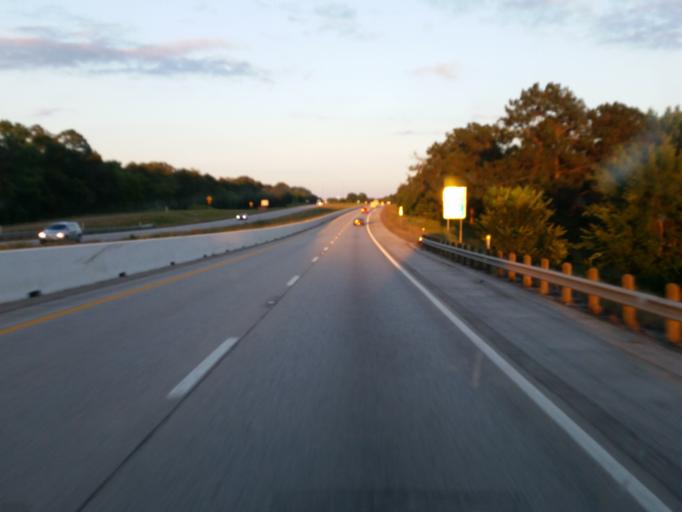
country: US
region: Texas
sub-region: Smith County
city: Hideaway
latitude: 32.4880
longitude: -95.5428
